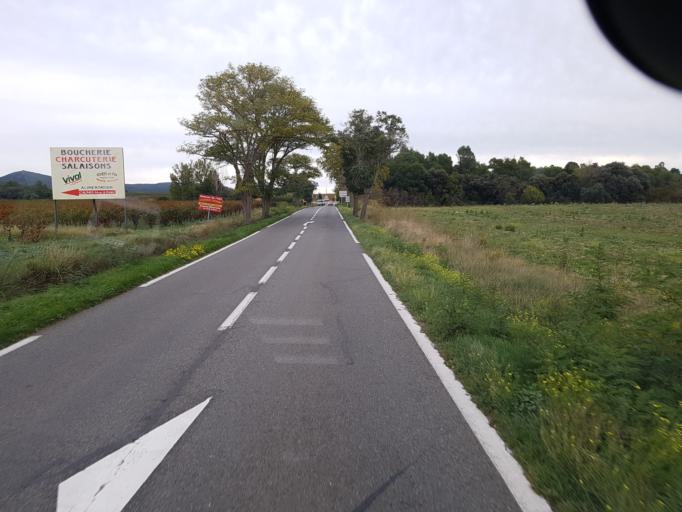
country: FR
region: Languedoc-Roussillon
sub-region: Departement de l'Aude
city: Caunes-Minervois
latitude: 43.3123
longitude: 2.4980
